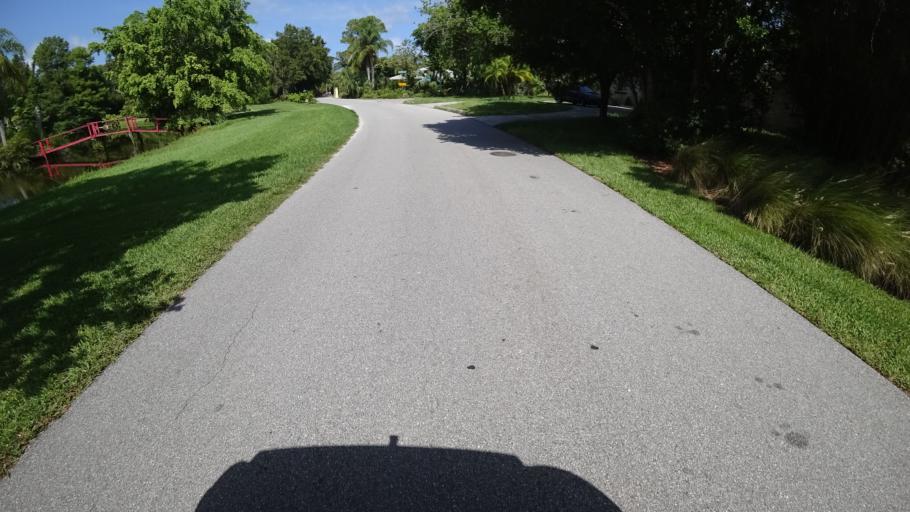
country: US
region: Florida
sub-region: Manatee County
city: Whitfield
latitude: 27.3892
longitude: -82.5634
